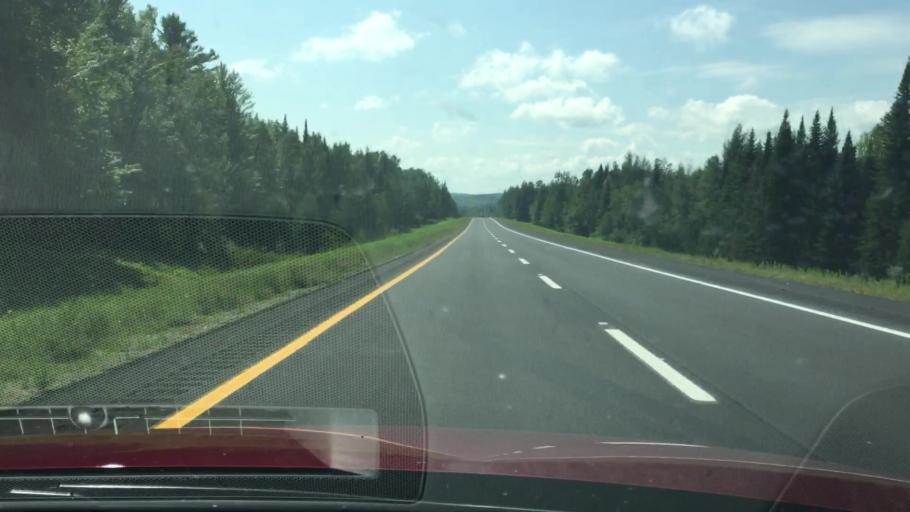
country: US
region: Maine
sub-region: Penobscot County
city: Patten
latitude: 45.9020
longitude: -68.3892
